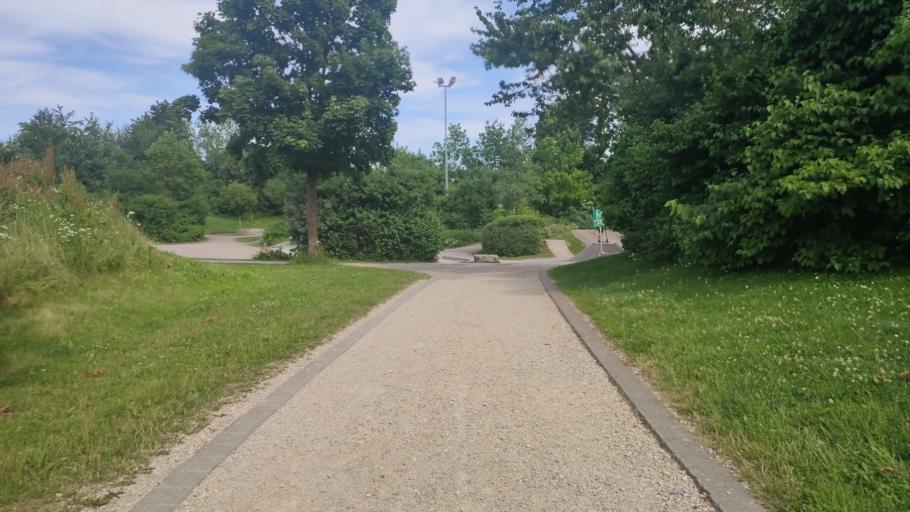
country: DE
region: Bavaria
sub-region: Swabia
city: Konigsbrunn
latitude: 48.2712
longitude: 10.8824
